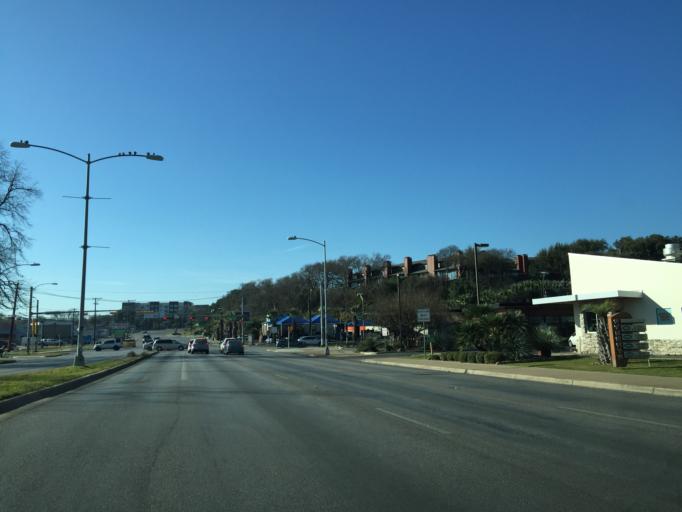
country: US
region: Texas
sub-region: Travis County
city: Austin
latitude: 30.2618
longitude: -97.7582
